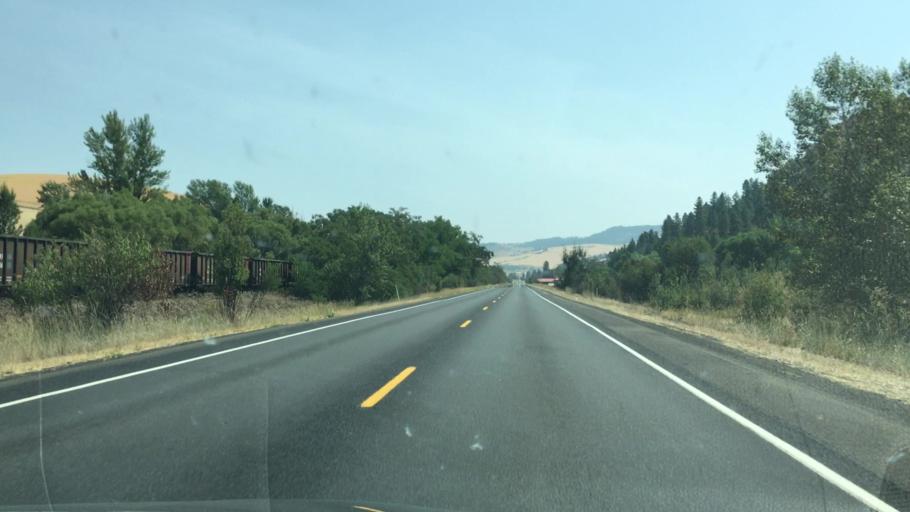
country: US
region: Idaho
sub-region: Nez Perce County
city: Lapwai
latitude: 46.3719
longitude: -116.7119
